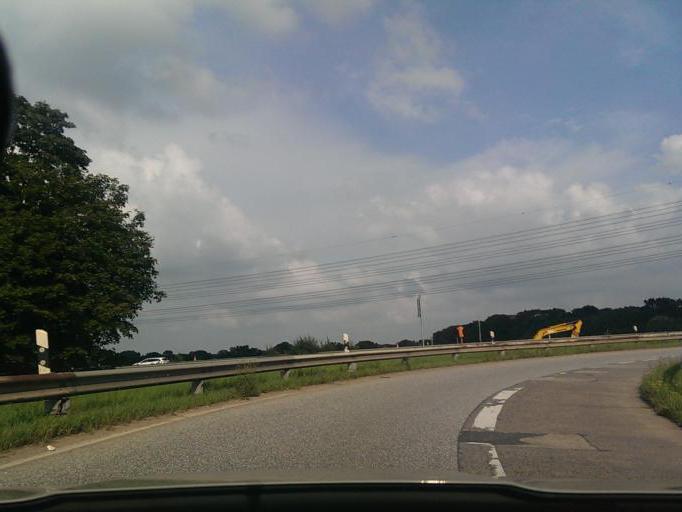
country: DE
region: Schleswig-Holstein
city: Bonningstedt
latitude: 53.6468
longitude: 9.9293
